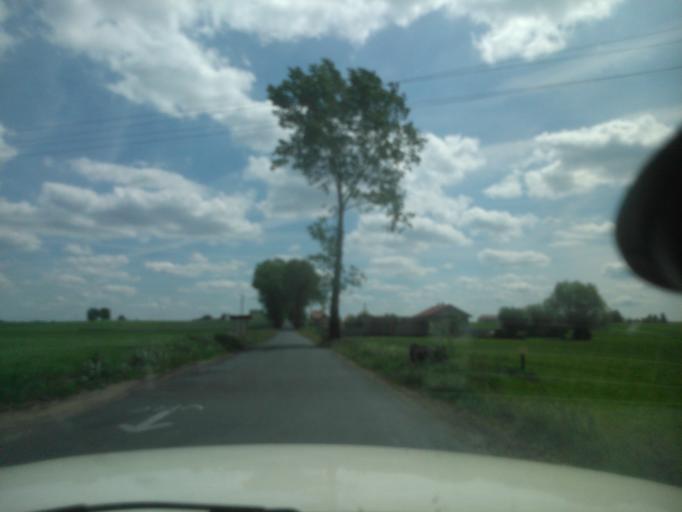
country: PL
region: Kujawsko-Pomorskie
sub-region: Powiat torunski
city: Obrowo
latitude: 53.0278
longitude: 18.8425
